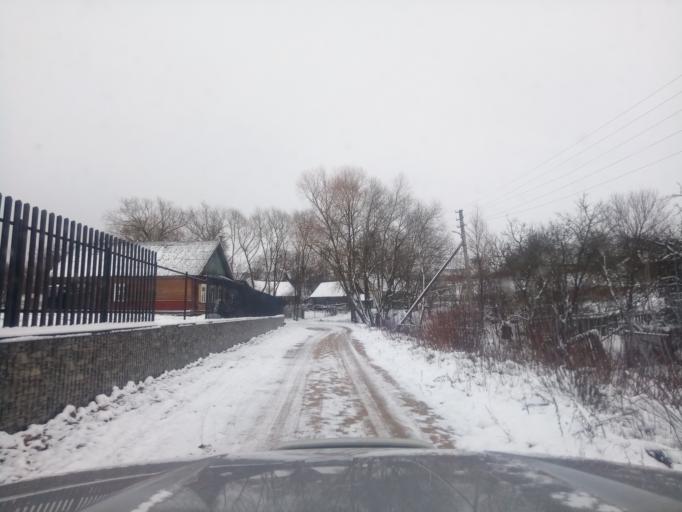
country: BY
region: Minsk
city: Kapyl'
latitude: 53.1562
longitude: 27.0802
